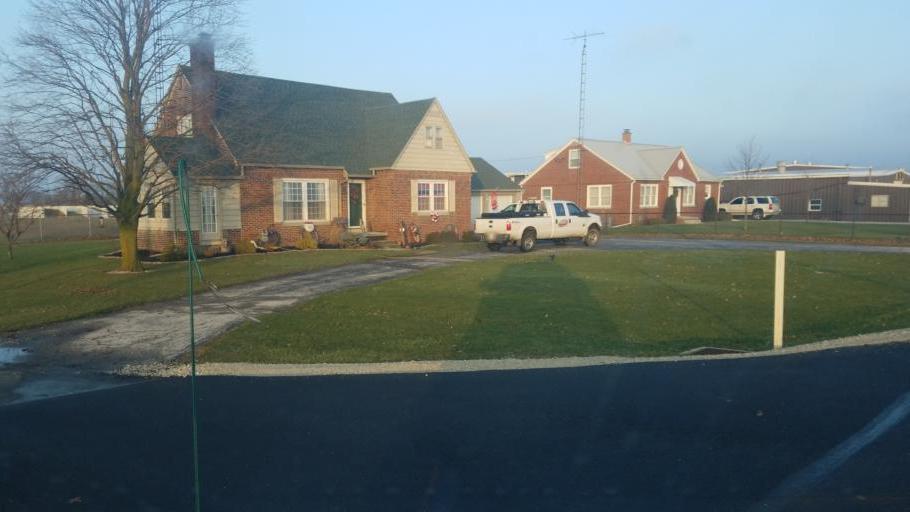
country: US
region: Ohio
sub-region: Wyandot County
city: Carey
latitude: 40.9581
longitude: -83.4059
